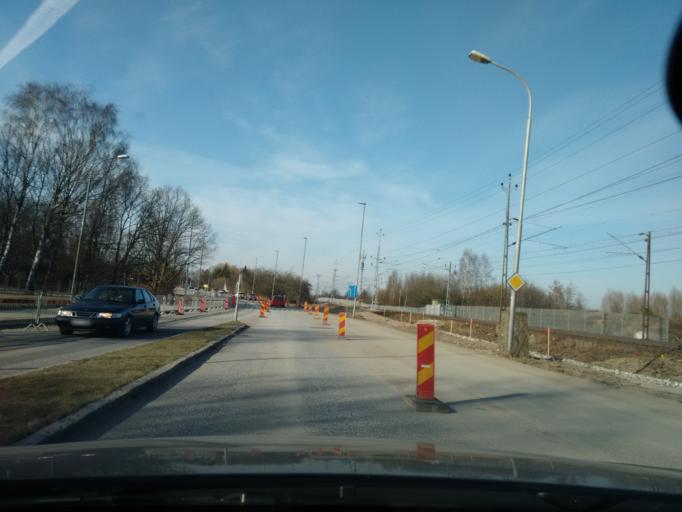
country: SE
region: Skane
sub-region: Lunds Kommun
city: Lund
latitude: 55.7227
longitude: 13.1832
